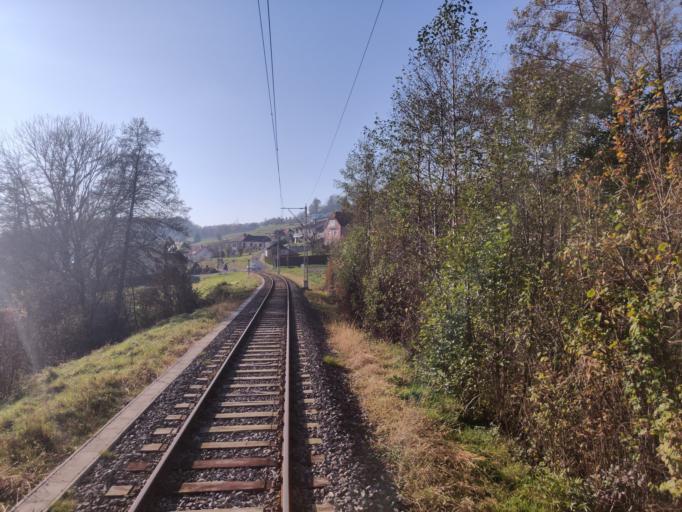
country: AT
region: Styria
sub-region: Politischer Bezirk Suedoststeiermark
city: Feldbach
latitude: 46.9454
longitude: 15.8860
